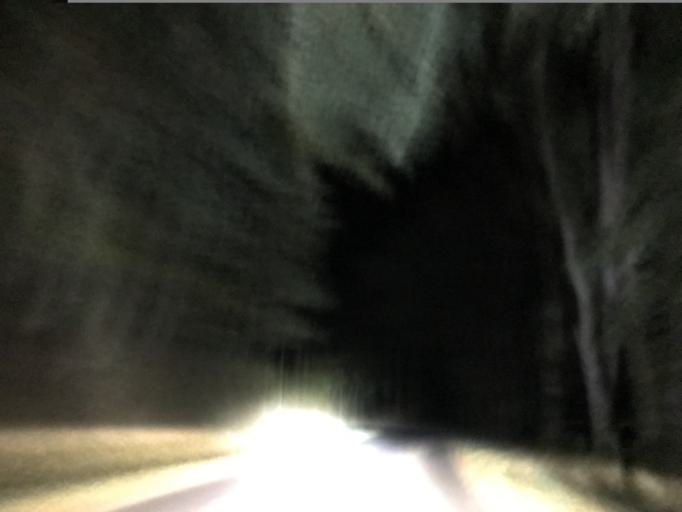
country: FR
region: Auvergne
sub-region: Departement du Puy-de-Dome
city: La Monnerie-le-Montel
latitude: 45.8671
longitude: 3.6135
